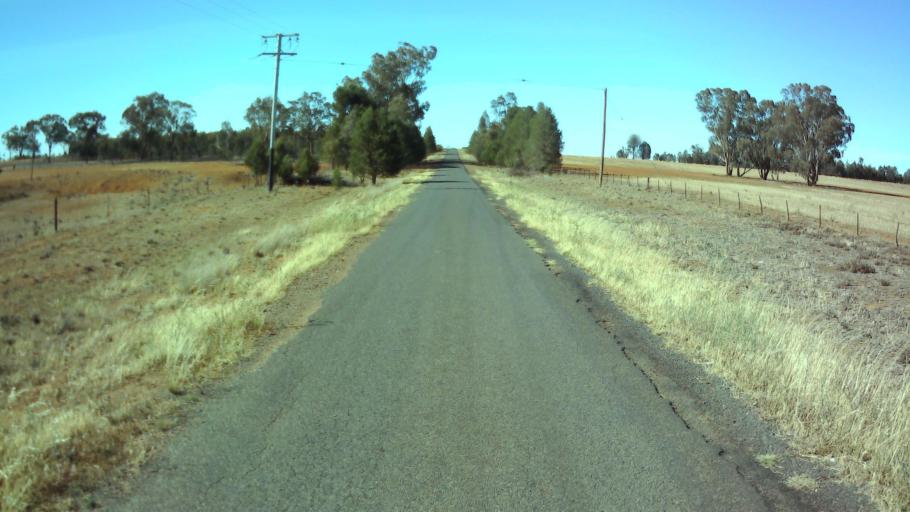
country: AU
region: New South Wales
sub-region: Weddin
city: Grenfell
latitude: -33.7588
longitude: 147.8299
